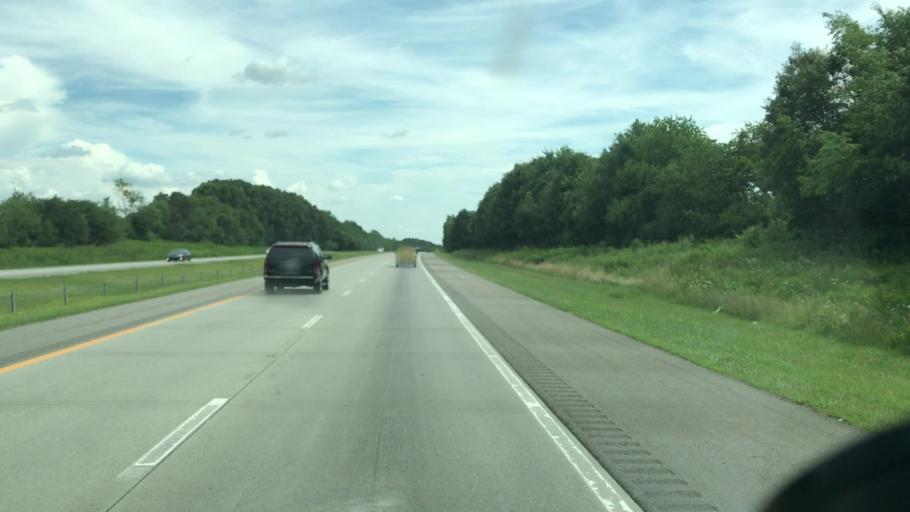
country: US
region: North Carolina
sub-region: Yadkin County
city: Jonesville
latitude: 36.1494
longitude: -80.8082
